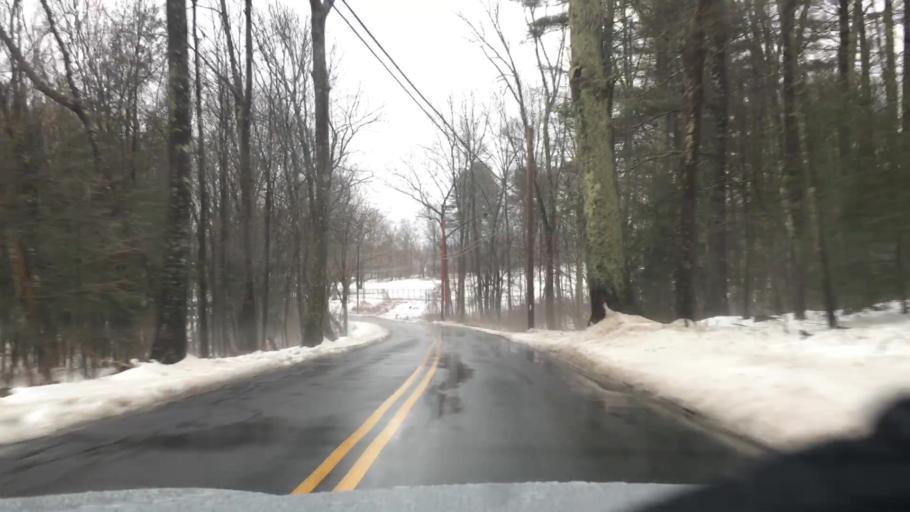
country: US
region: Massachusetts
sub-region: Hampshire County
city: Belchertown
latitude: 42.2814
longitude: -72.4282
